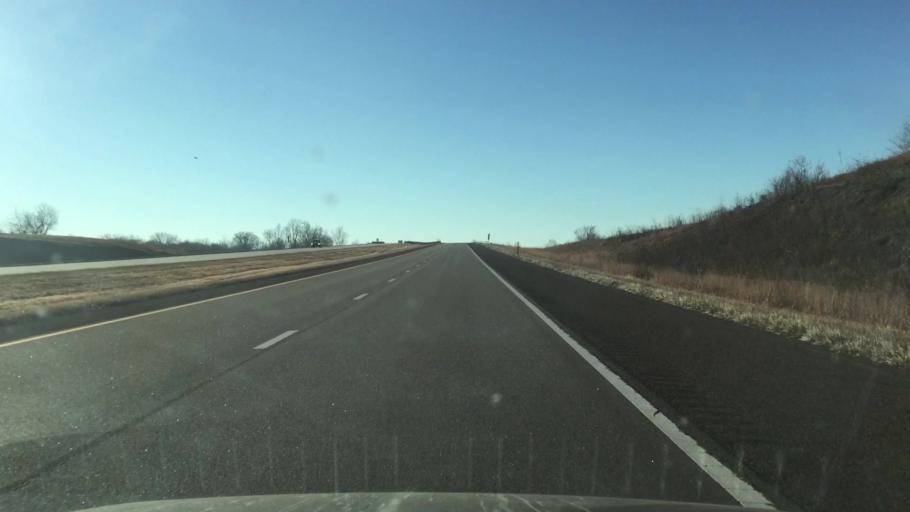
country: US
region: Kansas
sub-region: Miami County
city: Paola
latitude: 38.6392
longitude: -94.8360
